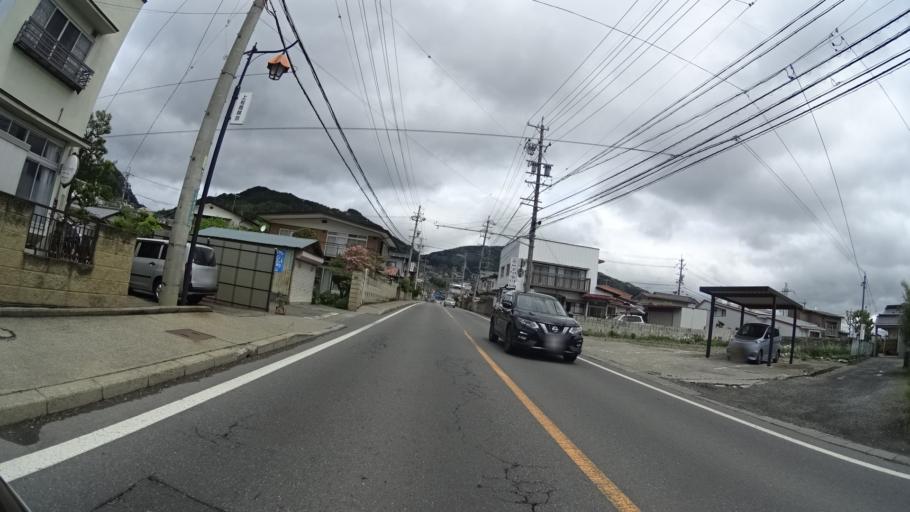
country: JP
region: Nagano
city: Nagano-shi
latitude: 36.6783
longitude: 138.2004
